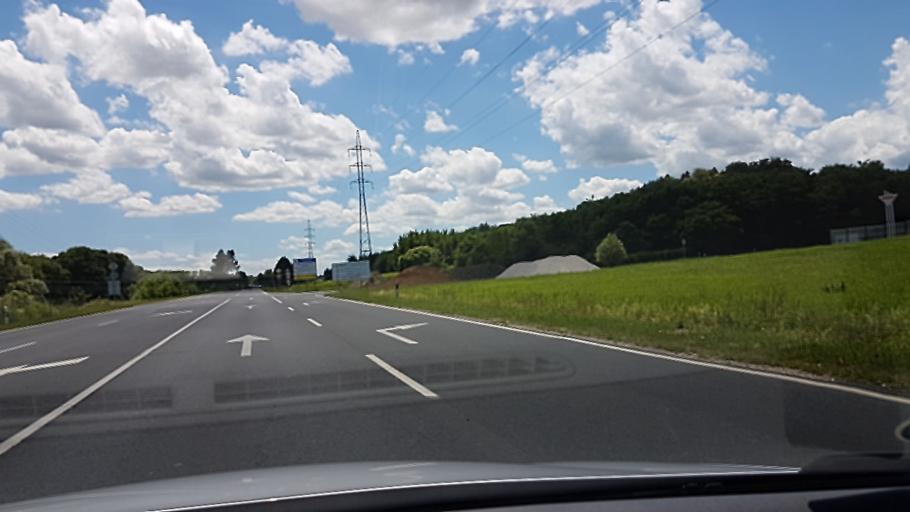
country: HU
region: Zala
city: Zalaegerszeg
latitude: 46.8303
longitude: 16.8638
